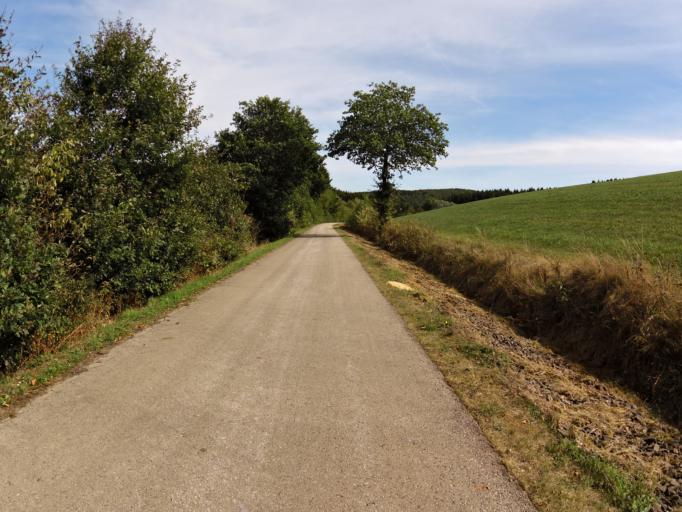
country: DE
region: Rheinland-Pfalz
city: Euscheid
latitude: 50.1265
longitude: 6.2903
